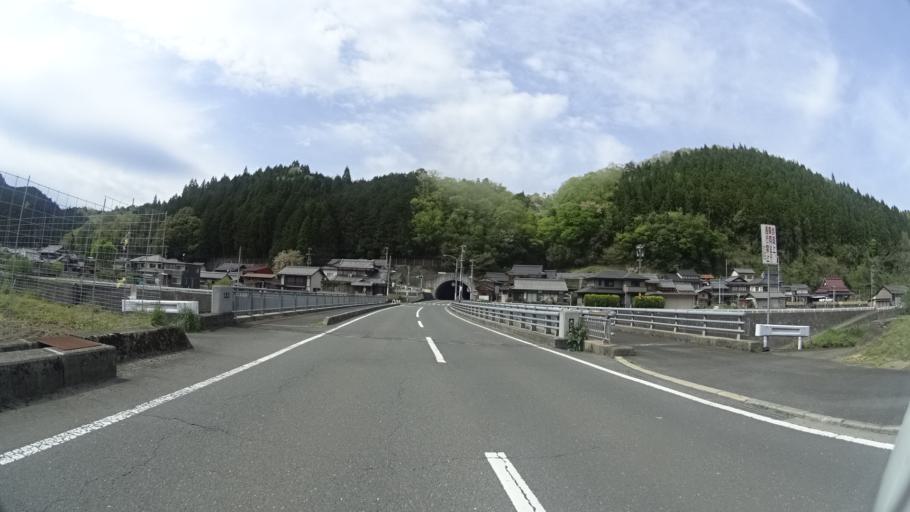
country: JP
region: Kyoto
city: Kameoka
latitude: 35.1531
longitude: 135.5085
